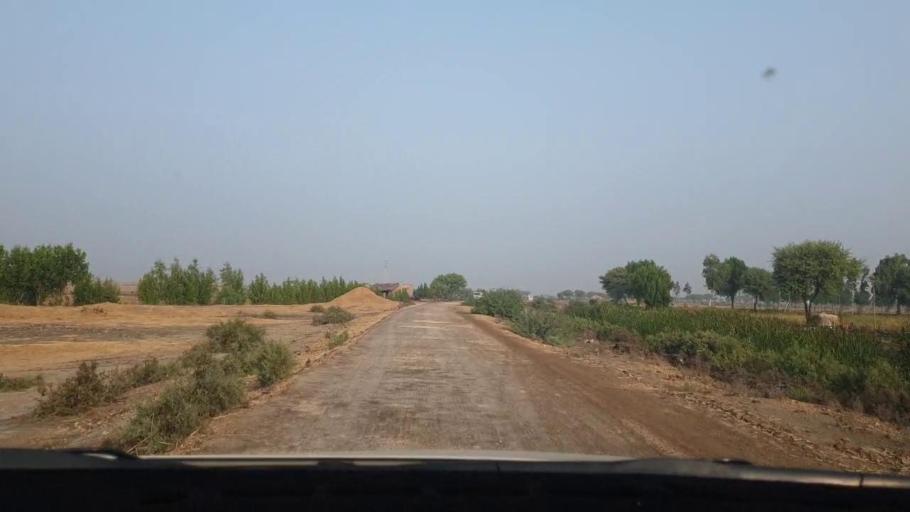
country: PK
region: Sindh
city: Tando Muhammad Khan
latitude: 25.0803
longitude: 68.4868
